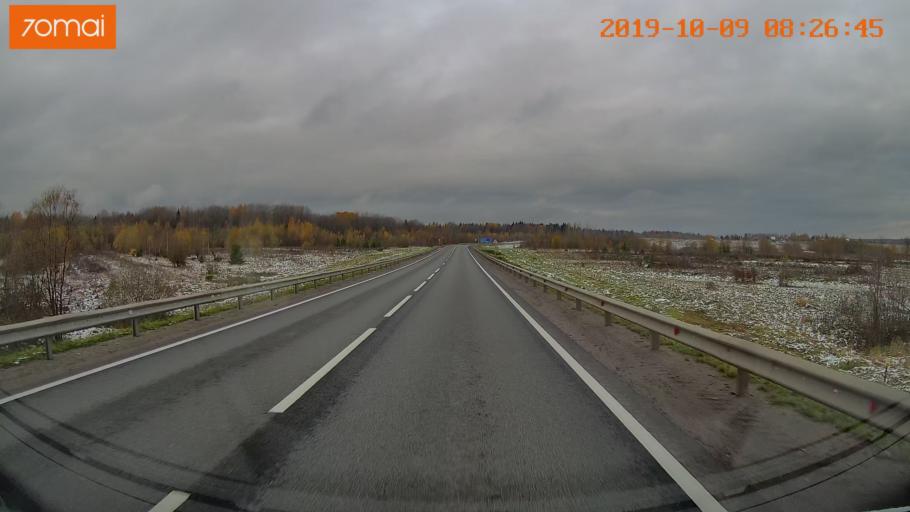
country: RU
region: Vologda
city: Gryazovets
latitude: 58.7964
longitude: 40.2610
